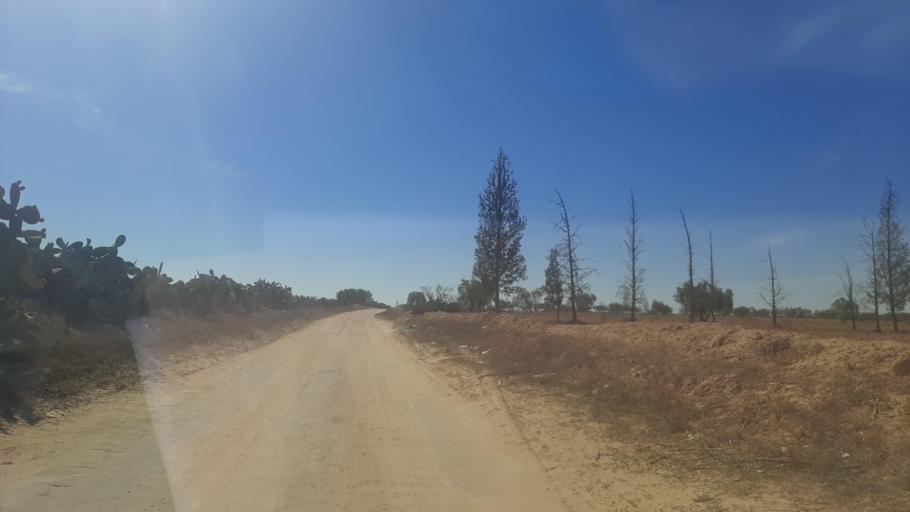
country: TN
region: Safaqis
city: Sfax
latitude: 34.8489
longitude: 10.5619
